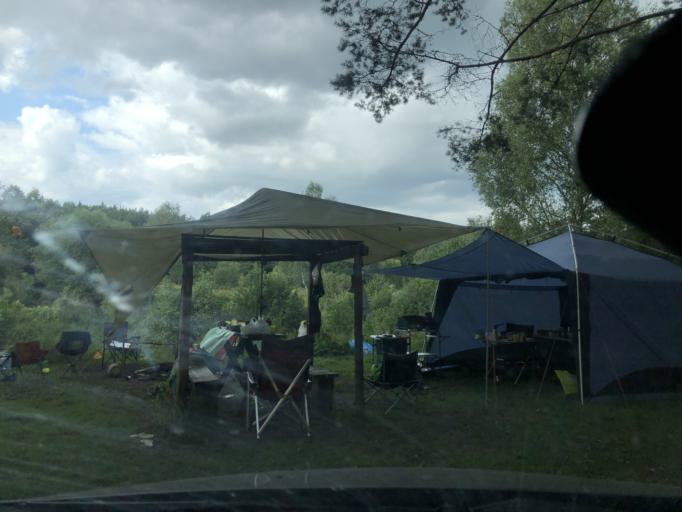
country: RU
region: Kaluga
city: Yukhnov
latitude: 54.7272
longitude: 35.1149
